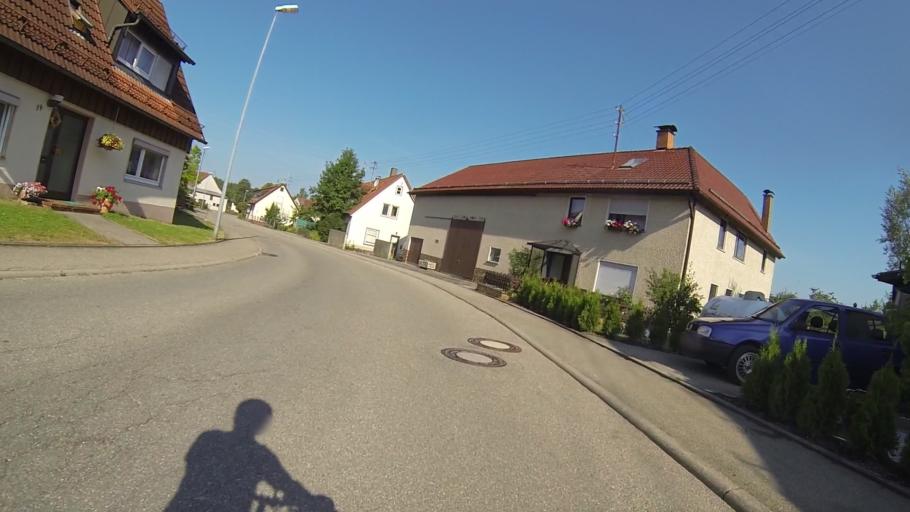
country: DE
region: Baden-Wuerttemberg
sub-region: Regierungsbezirk Stuttgart
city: Konigsbronn
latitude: 48.7481
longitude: 10.1440
